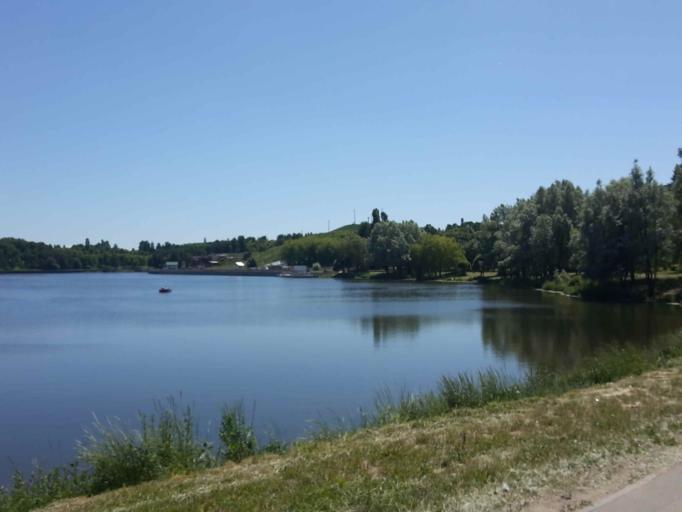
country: BY
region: Minsk
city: Syenitsa
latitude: 53.8530
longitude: 27.5122
